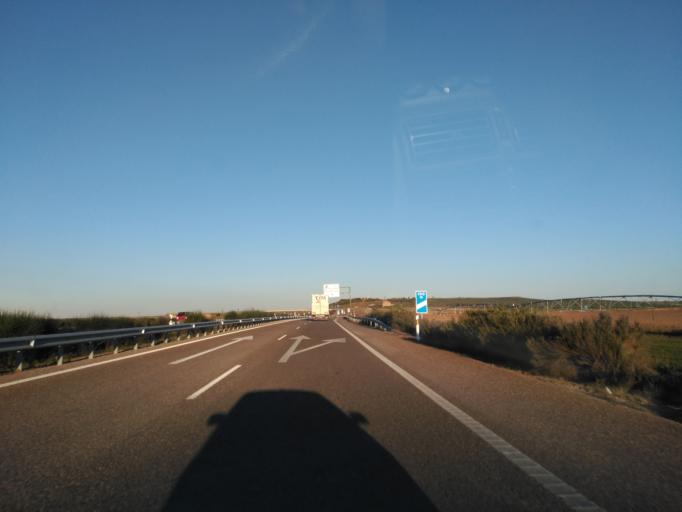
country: ES
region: Castille and Leon
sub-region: Provincia de Valladolid
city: Alaejos
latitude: 41.3196
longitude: -5.2101
